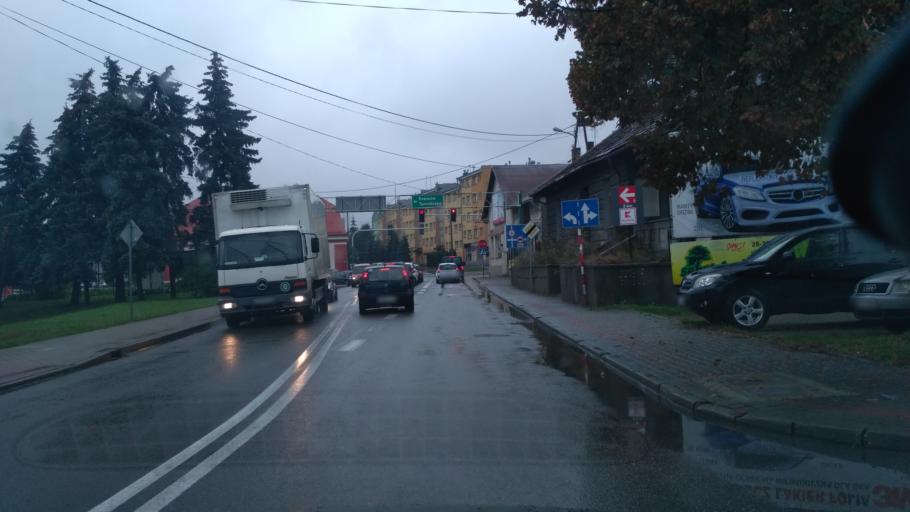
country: PL
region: Subcarpathian Voivodeship
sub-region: Powiat debicki
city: Debica
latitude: 50.0523
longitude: 21.4113
